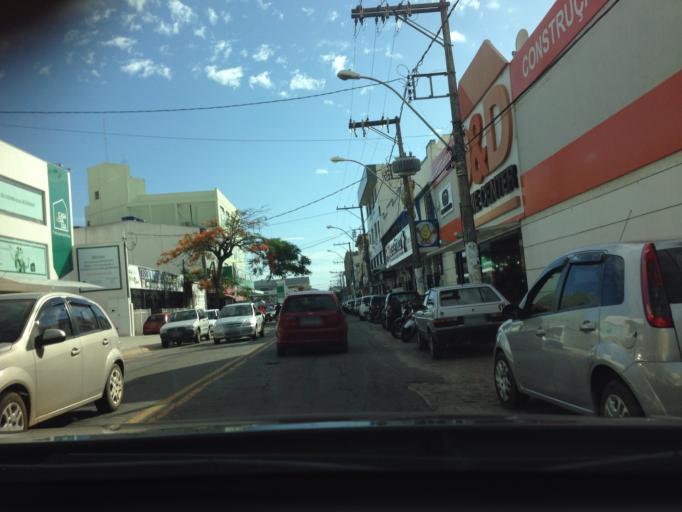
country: BR
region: Espirito Santo
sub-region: Guarapari
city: Guarapari
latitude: -20.6624
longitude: -40.4991
